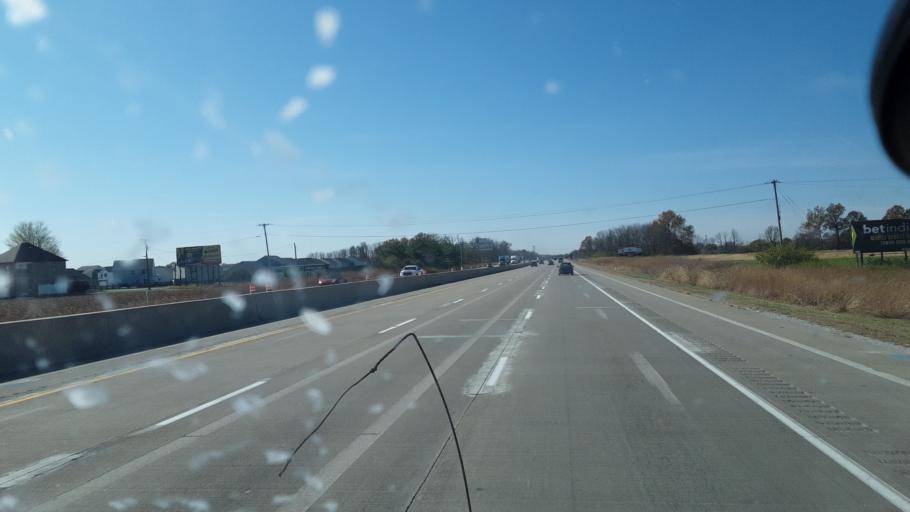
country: US
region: Indiana
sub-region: Marion County
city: Cumberland
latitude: 39.8110
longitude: -85.9425
